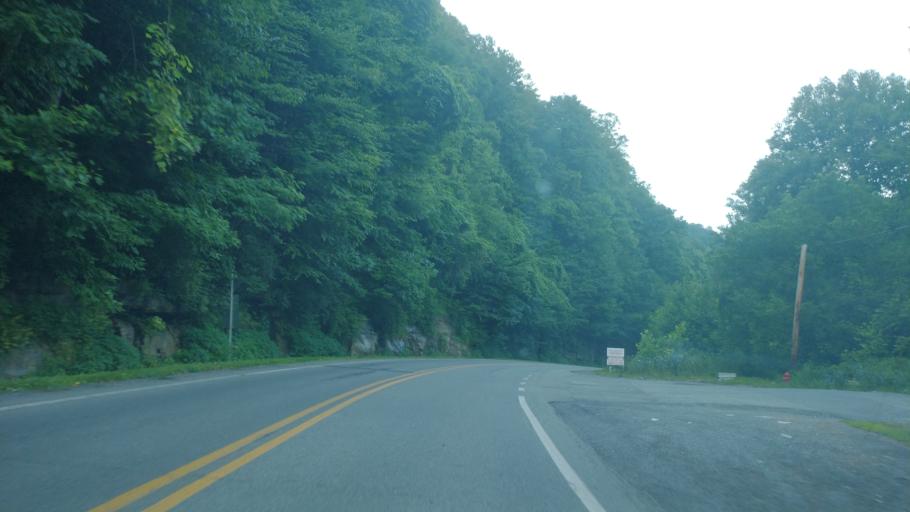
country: US
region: West Virginia
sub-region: Mercer County
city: Bluewell
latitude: 37.3841
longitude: -81.4137
